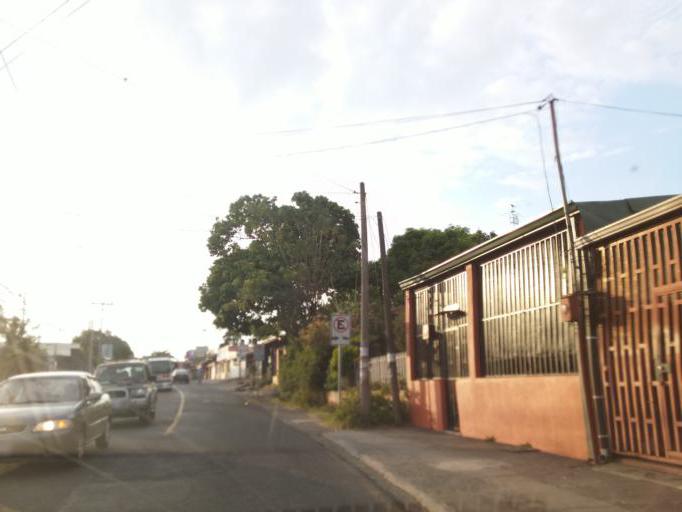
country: CR
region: Alajuela
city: Alajuela
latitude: 10.0047
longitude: -84.2259
